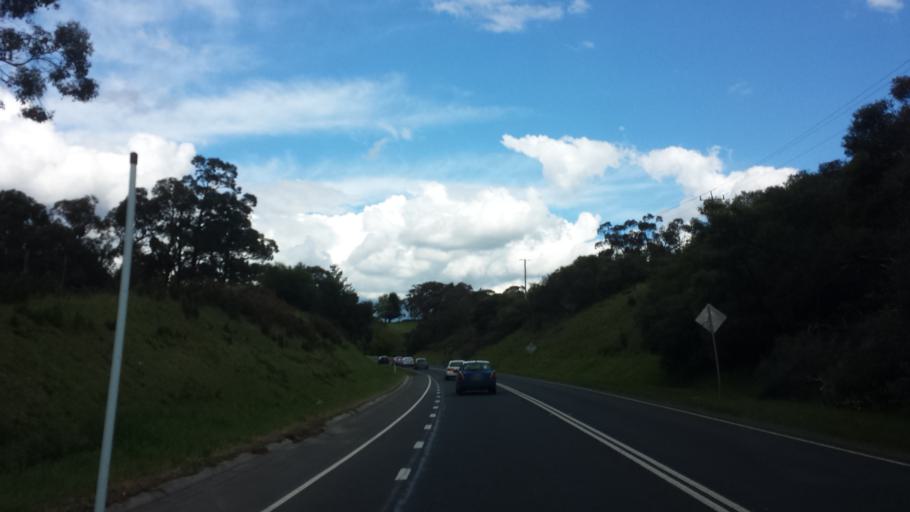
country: AU
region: Victoria
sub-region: Yarra Ranges
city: Selby
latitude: -37.9388
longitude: 145.3925
